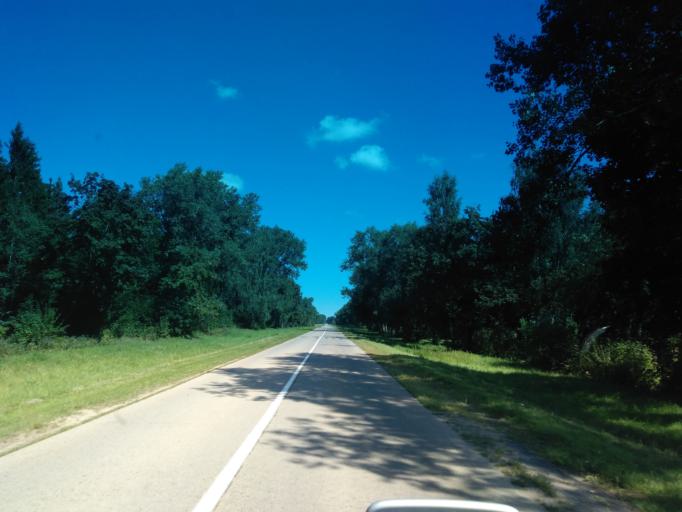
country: BY
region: Minsk
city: Stan'kava
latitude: 53.6436
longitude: 27.2944
